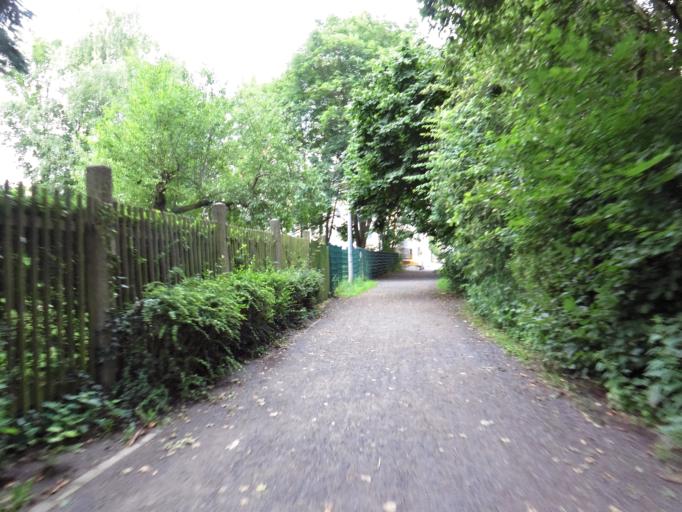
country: DE
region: Saxony
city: Leipzig
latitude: 51.3221
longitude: 12.4256
